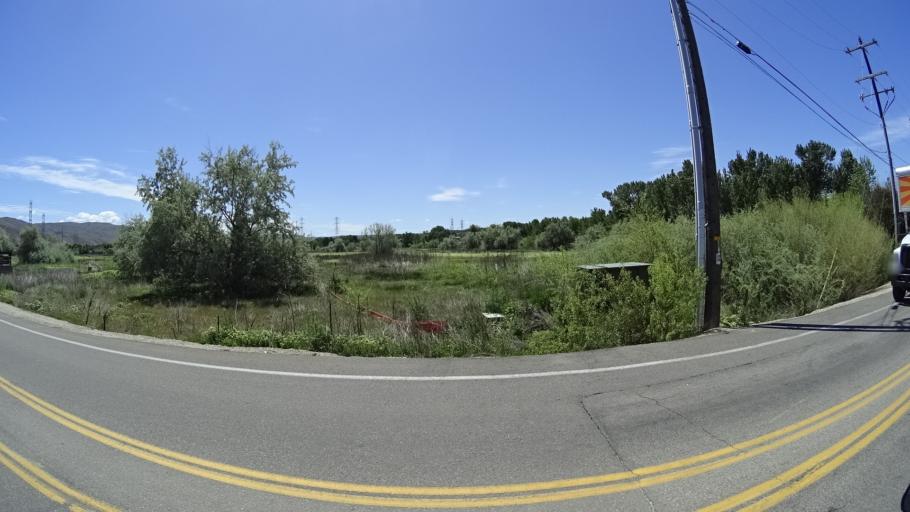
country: US
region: Idaho
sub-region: Ada County
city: Boise
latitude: 43.5665
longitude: -116.1310
